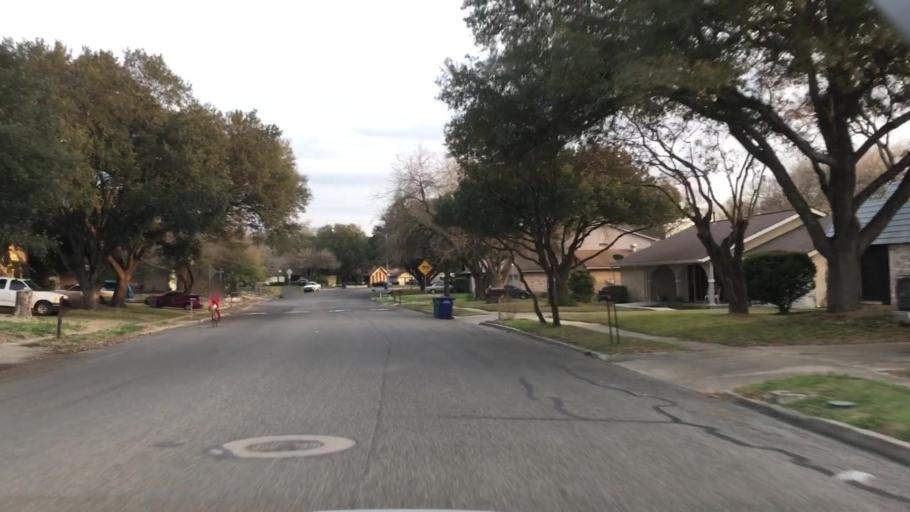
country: US
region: Texas
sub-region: Bexar County
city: Windcrest
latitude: 29.5576
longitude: -98.3930
